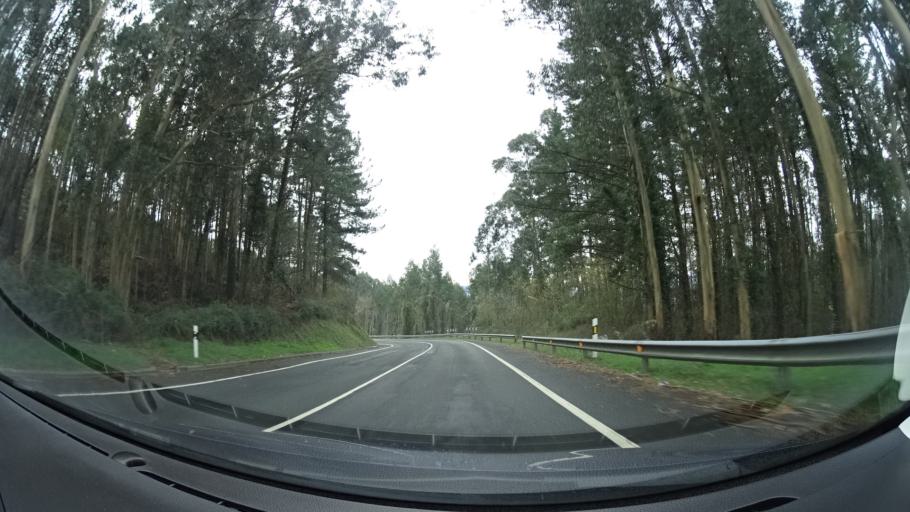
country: ES
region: Basque Country
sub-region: Bizkaia
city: Bakio
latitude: 43.3850
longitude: -2.7873
